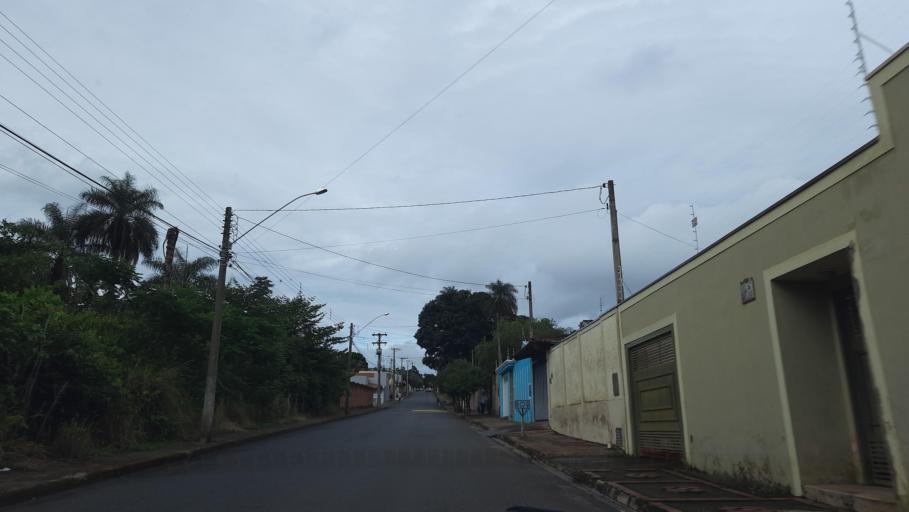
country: BR
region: Sao Paulo
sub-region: Casa Branca
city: Casa Branca
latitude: -21.7815
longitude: -47.0872
